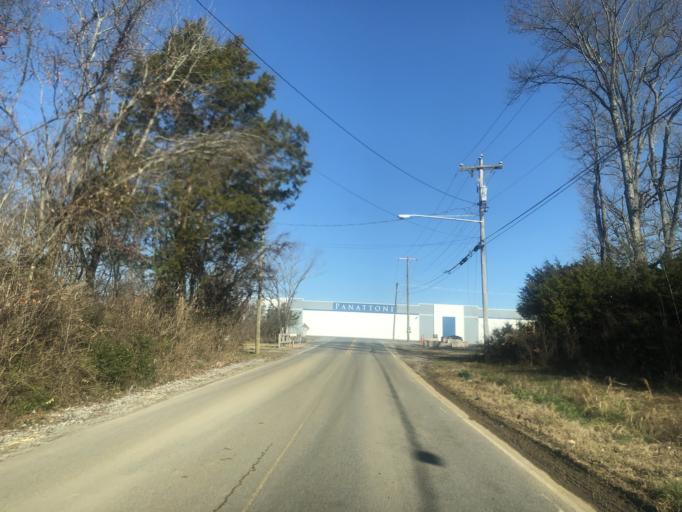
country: US
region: Tennessee
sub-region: Rutherford County
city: La Vergne
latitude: 36.0022
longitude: -86.5860
